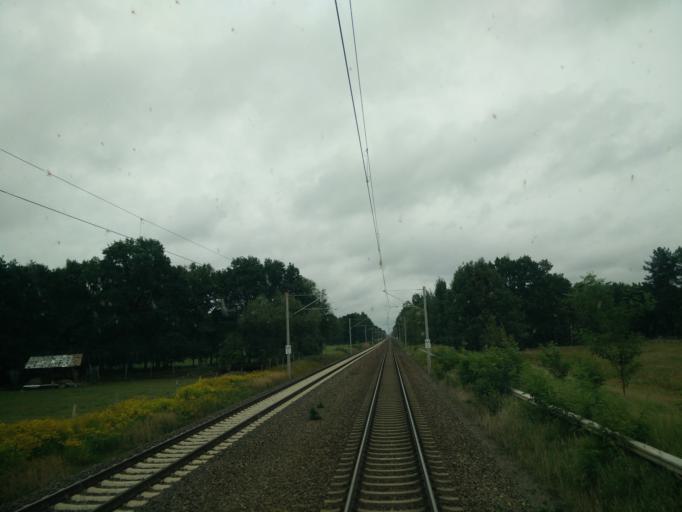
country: DE
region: Brandenburg
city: Kasel-Golzig
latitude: 51.9886
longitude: 13.7811
